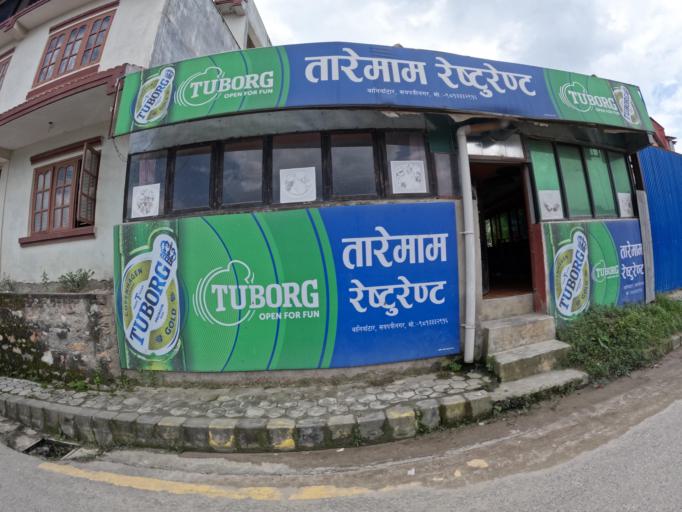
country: NP
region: Central Region
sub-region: Bagmati Zone
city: Kathmandu
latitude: 27.7473
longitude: 85.3151
